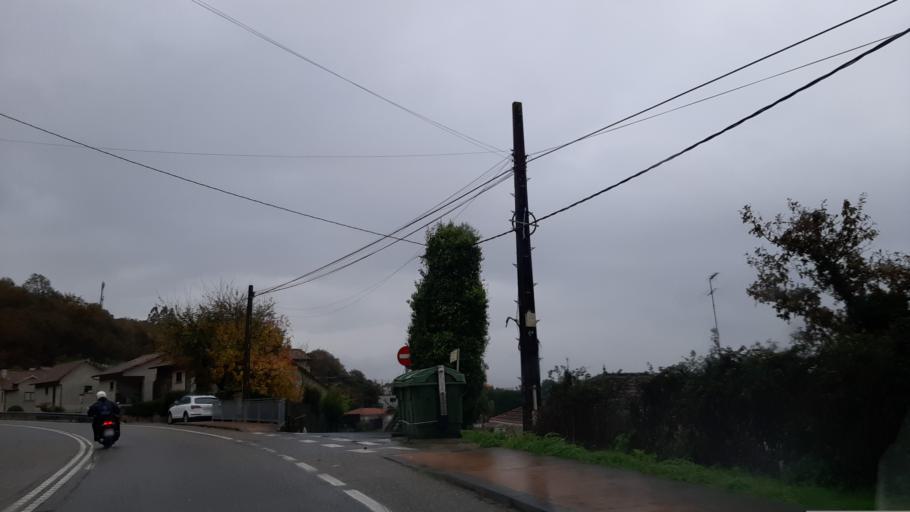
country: ES
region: Galicia
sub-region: Provincia de Pontevedra
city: Nigran
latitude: 42.1745
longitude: -8.7995
